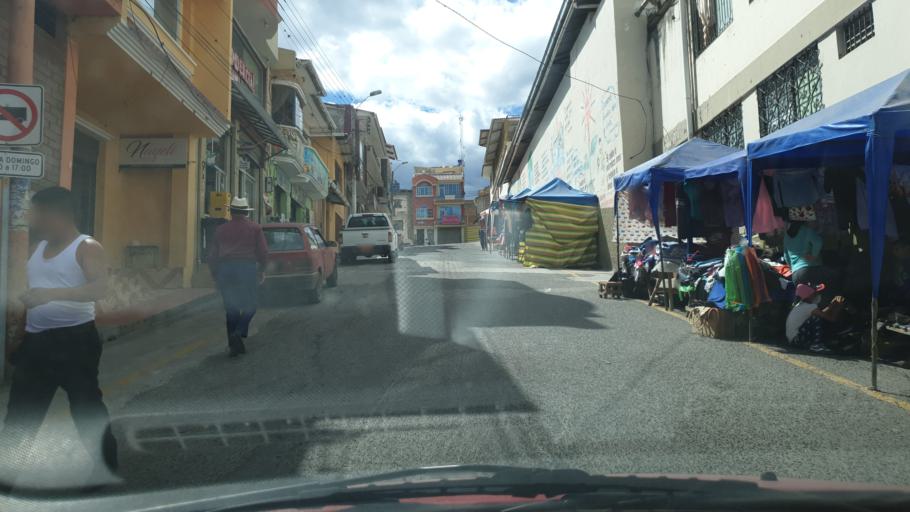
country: EC
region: Azuay
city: Cuenca
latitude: -3.2755
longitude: -79.3152
